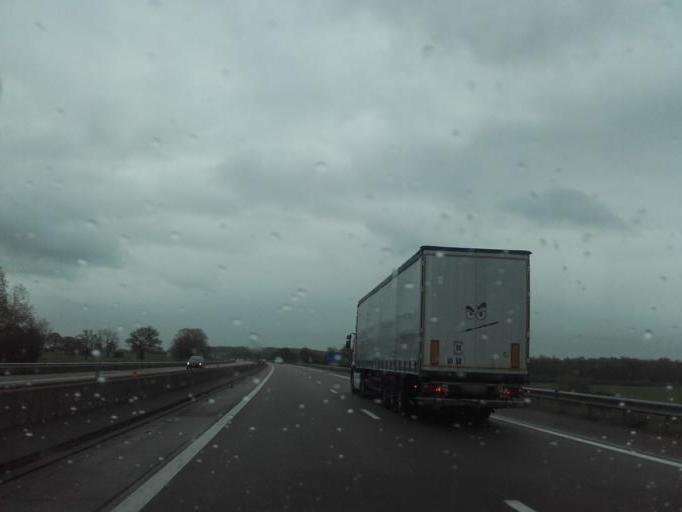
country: FR
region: Bourgogne
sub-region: Departement de l'Yonne
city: Avallon
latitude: 47.5086
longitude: 4.0040
